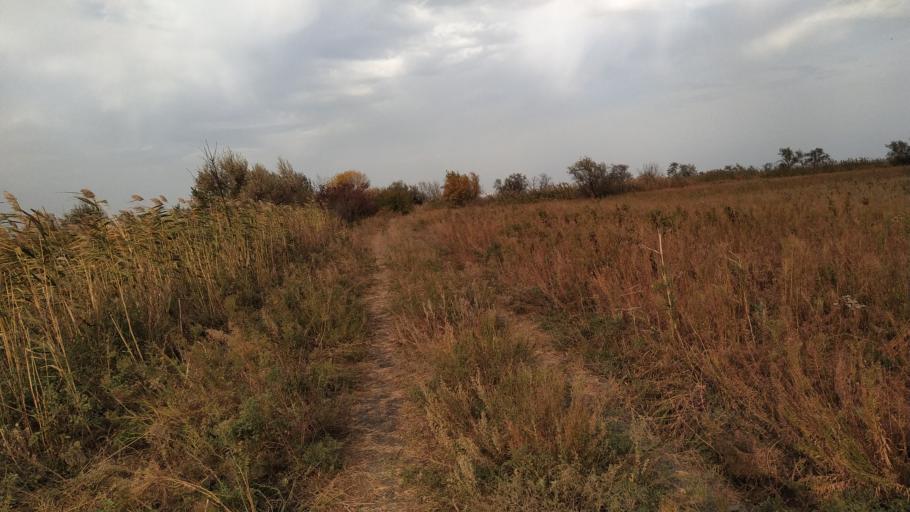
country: RU
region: Rostov
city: Kuleshovka
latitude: 47.1450
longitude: 39.5855
